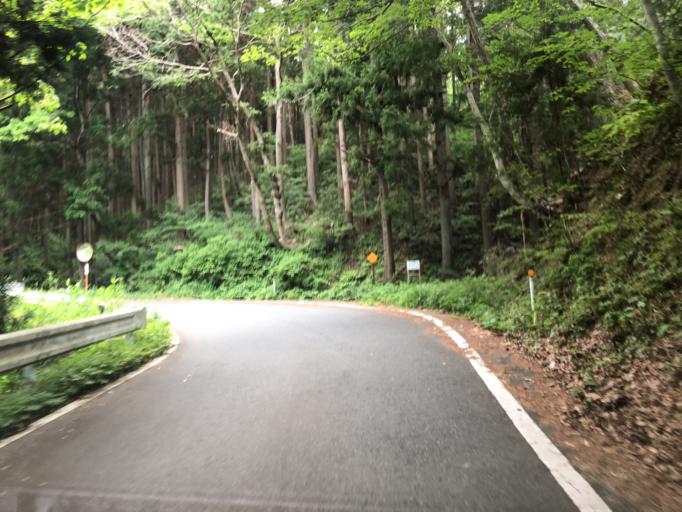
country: JP
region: Miyagi
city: Marumori
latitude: 37.8288
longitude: 140.8616
